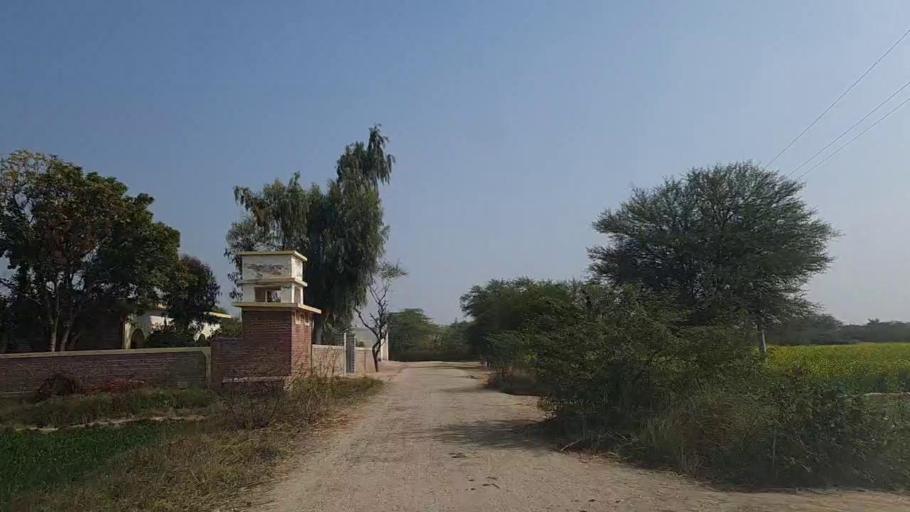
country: PK
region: Sindh
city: Daur
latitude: 26.4544
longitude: 68.4541
